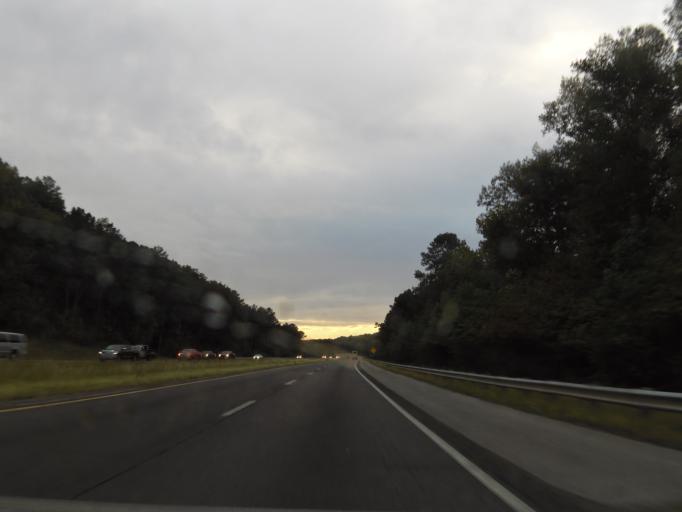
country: US
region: Alabama
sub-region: Saint Clair County
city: Margaret
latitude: 33.7271
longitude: -86.5004
